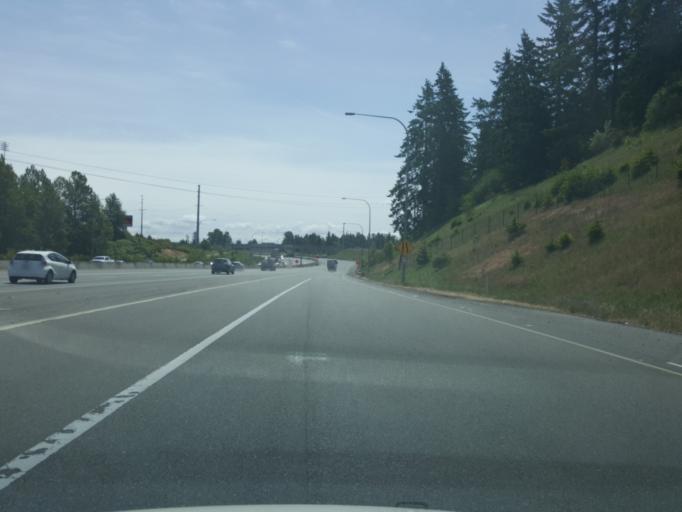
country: US
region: Washington
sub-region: Pierce County
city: Fircrest
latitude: 47.2400
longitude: -122.5026
